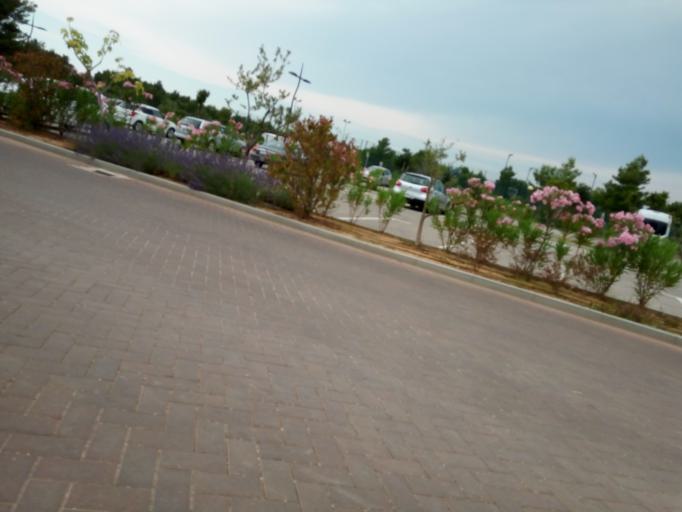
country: HR
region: Sibensko-Kniniska
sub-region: Grad Sibenik
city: Sibenik
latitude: 43.6966
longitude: 15.8854
